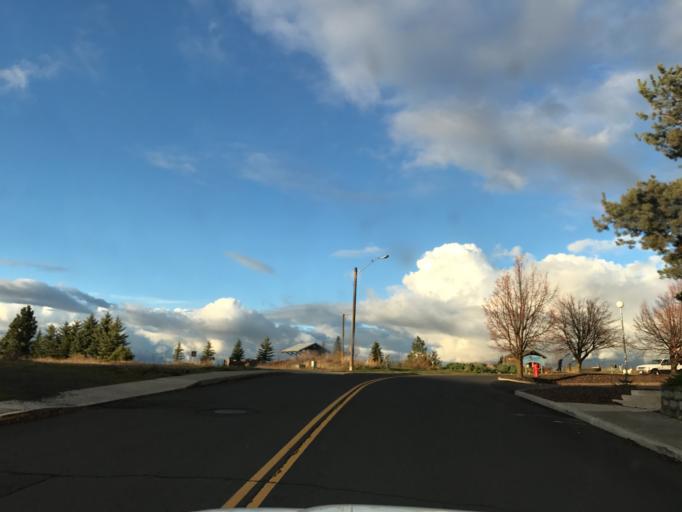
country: US
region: Idaho
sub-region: Latah County
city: Moscow
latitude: 46.7351
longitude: -117.0164
